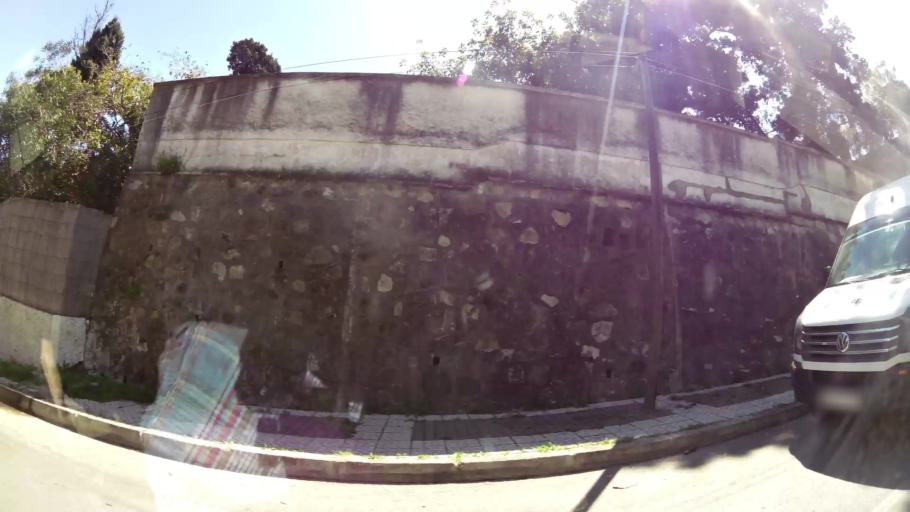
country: MA
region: Tanger-Tetouan
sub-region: Tanger-Assilah
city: Tangier
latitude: 35.7800
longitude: -5.8312
